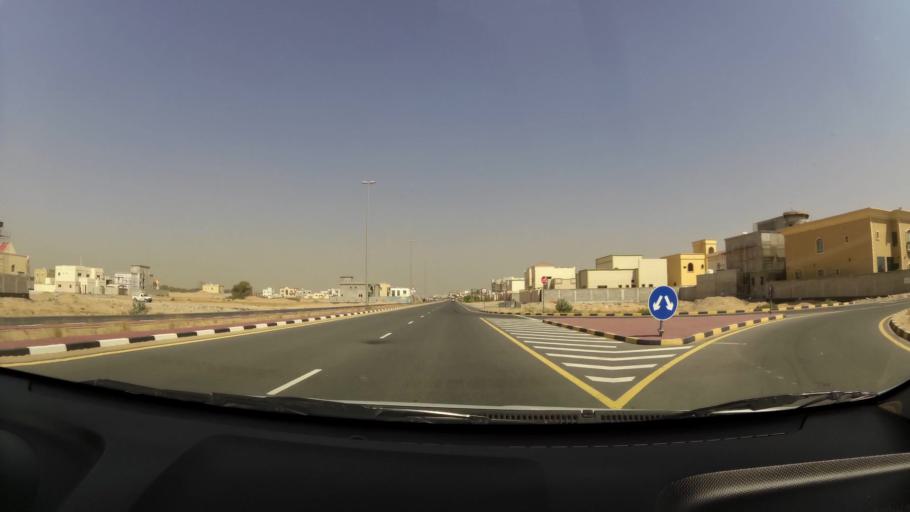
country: AE
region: Ajman
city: Ajman
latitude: 25.4027
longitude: 55.5426
